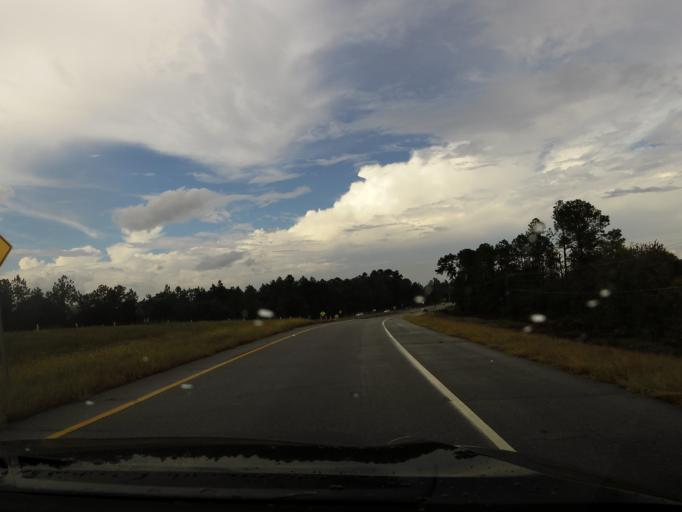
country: US
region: Georgia
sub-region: Wayne County
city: Jesup
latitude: 31.6238
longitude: -81.8671
